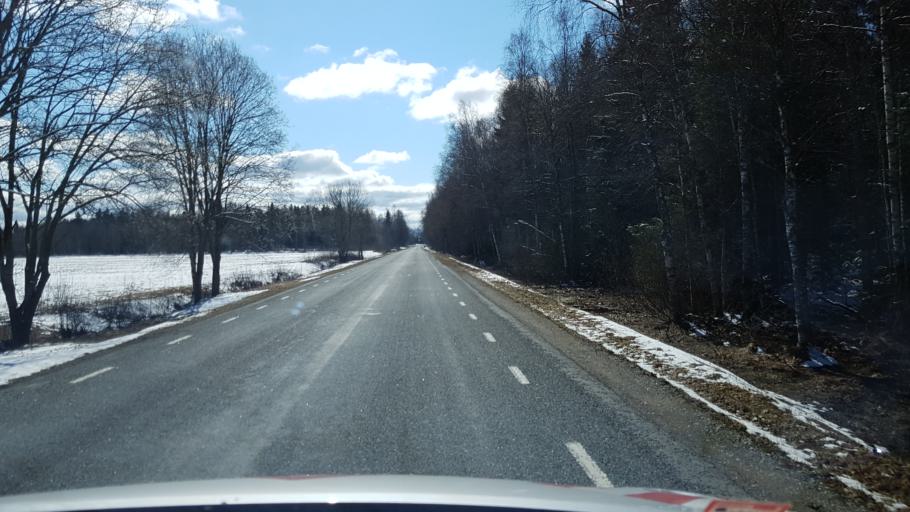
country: EE
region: Laeaene-Virumaa
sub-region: Kadrina vald
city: Kadrina
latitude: 59.4782
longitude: 25.9954
